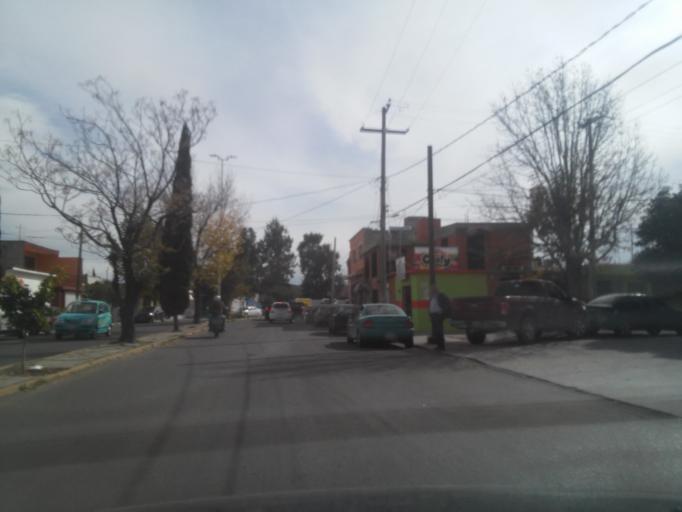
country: MX
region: Durango
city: Victoria de Durango
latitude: 24.0099
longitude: -104.6546
